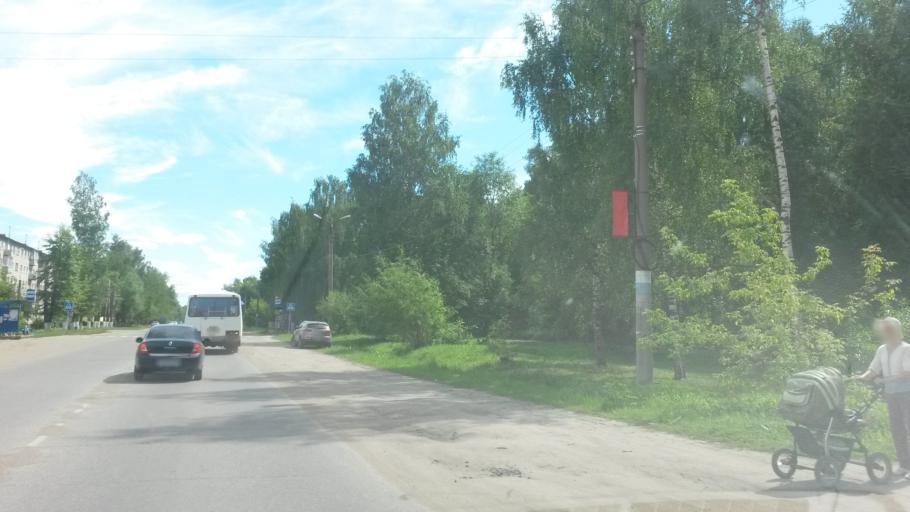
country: RU
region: Ivanovo
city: Zavolzhsk
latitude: 57.4875
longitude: 42.1418
